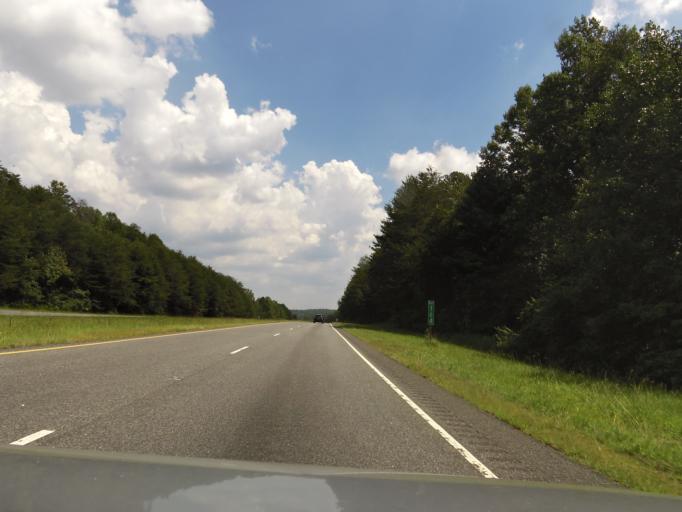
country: US
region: North Carolina
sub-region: Polk County
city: Columbus
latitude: 35.2699
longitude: -82.1605
